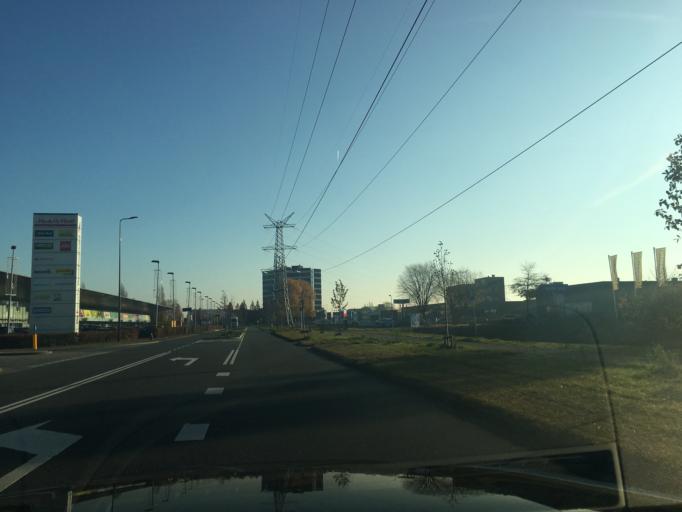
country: NL
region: North Brabant
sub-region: Gemeente 's-Hertogenbosch
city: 's-Hertogenbosch
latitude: 51.7088
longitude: 5.3342
